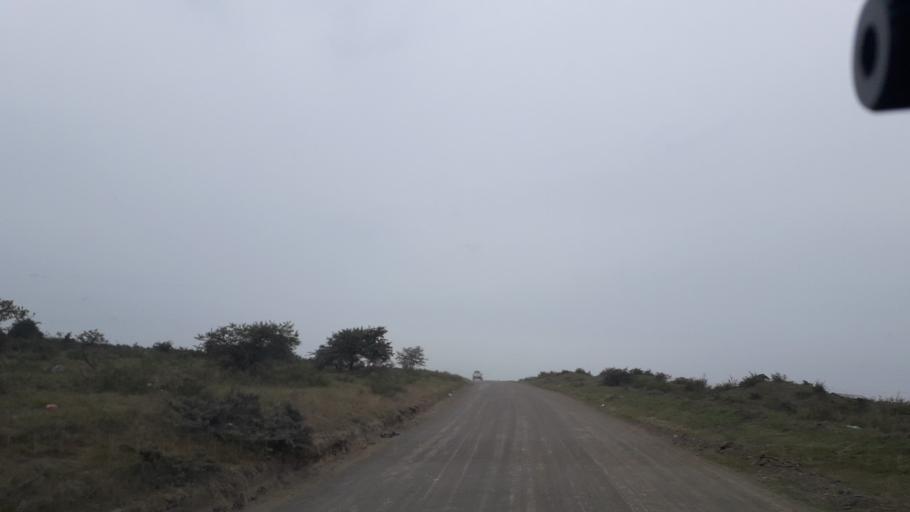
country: ZA
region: Eastern Cape
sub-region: Buffalo City Metropolitan Municipality
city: Bhisho
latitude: -32.7946
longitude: 27.3439
